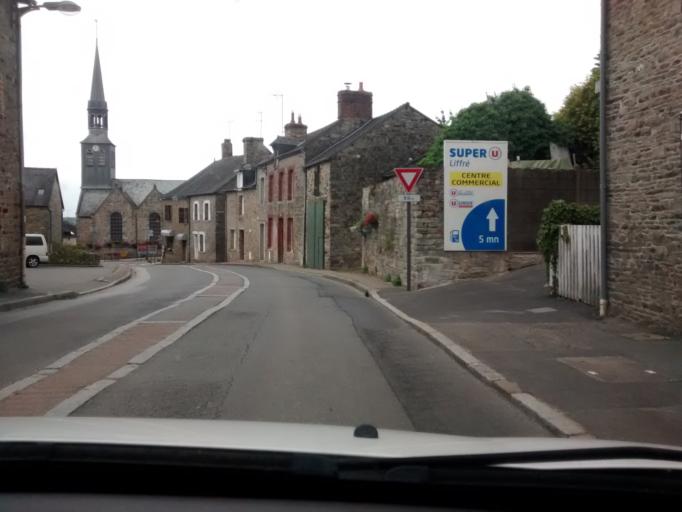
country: FR
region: Brittany
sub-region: Departement d'Ille-et-Vilaine
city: La Bouexiere
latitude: 48.1833
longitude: -1.4385
